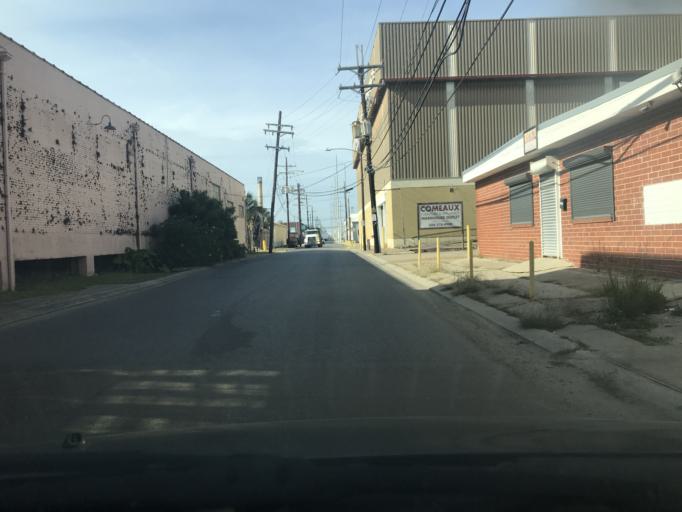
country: US
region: Louisiana
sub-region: Orleans Parish
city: New Orleans
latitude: 29.9562
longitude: -90.0961
